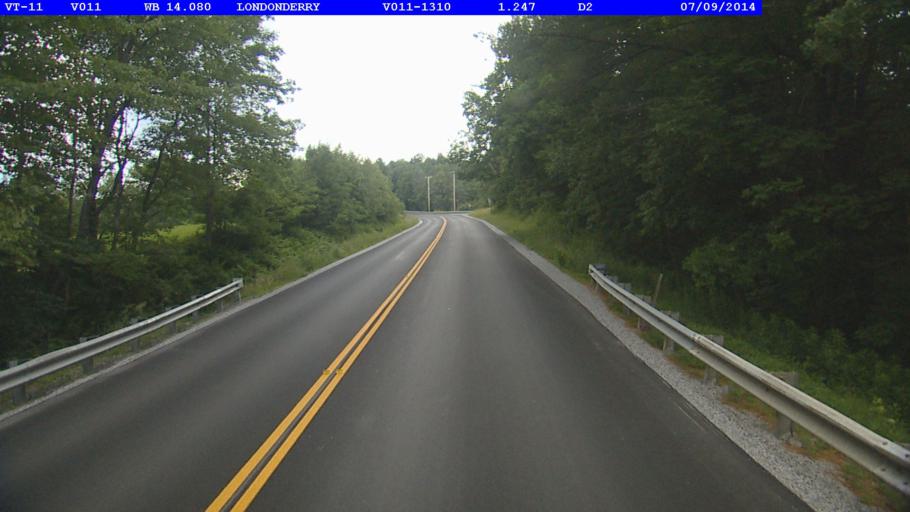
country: US
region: Vermont
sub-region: Windsor County
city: Chester
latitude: 43.2325
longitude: -72.8265
